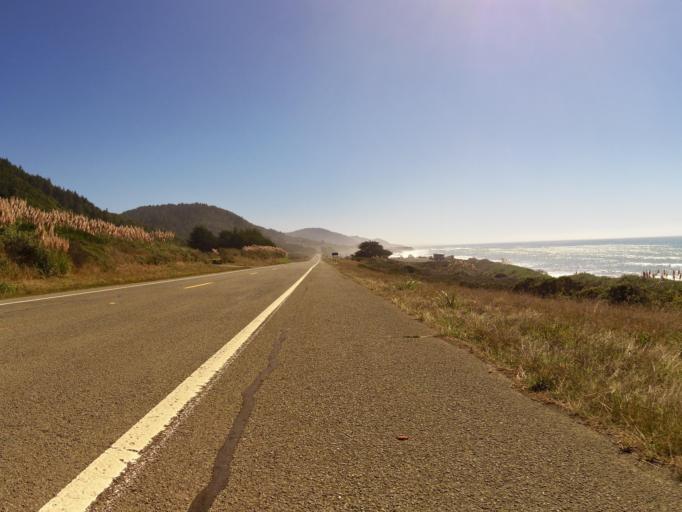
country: US
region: California
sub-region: Mendocino County
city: Fort Bragg
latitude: 39.6879
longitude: -123.7927
